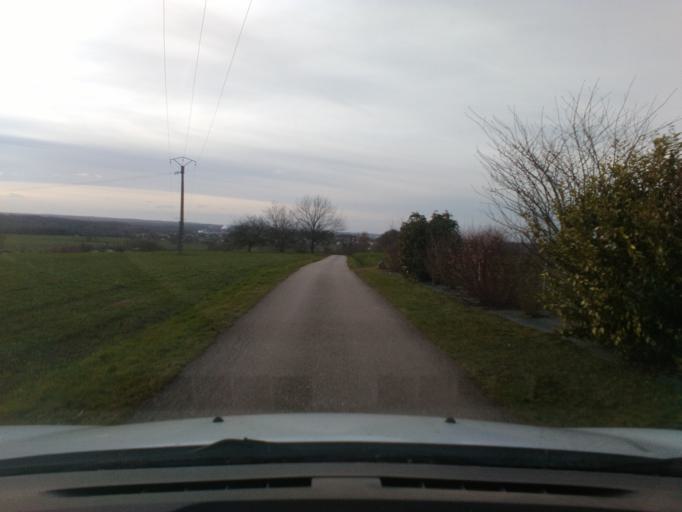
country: FR
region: Lorraine
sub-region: Departement des Vosges
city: Jeanmenil
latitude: 48.3289
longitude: 6.7104
